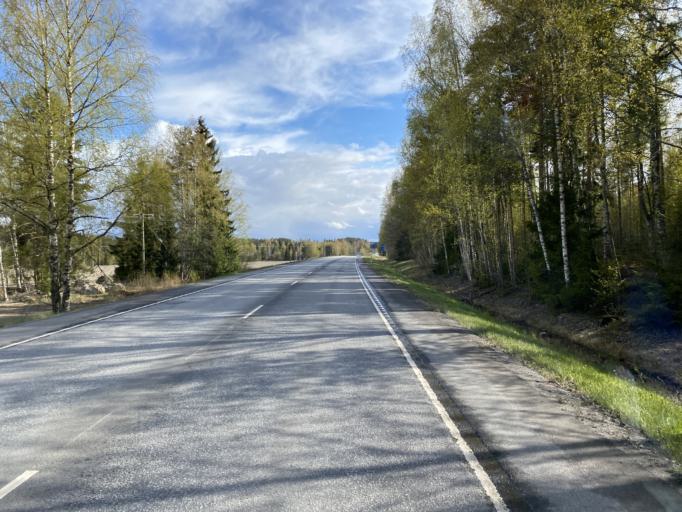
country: FI
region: Pirkanmaa
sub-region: Tampere
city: Lempaeaelae
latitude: 61.2718
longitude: 23.7474
